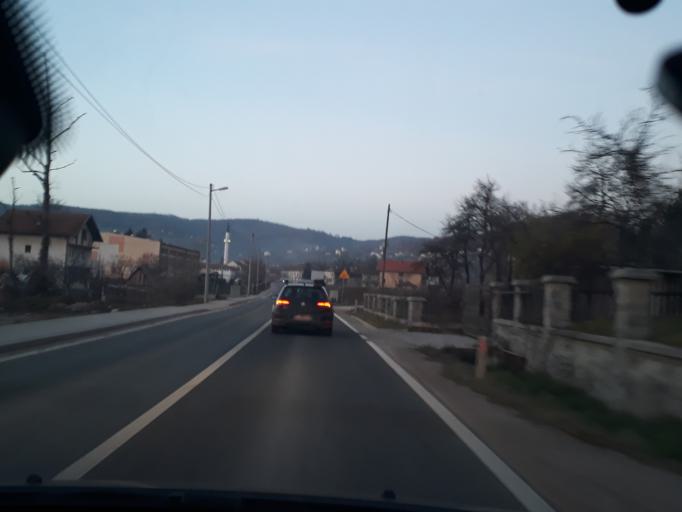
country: BA
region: Federation of Bosnia and Herzegovina
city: Hadzici
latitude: 43.8741
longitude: 18.2065
